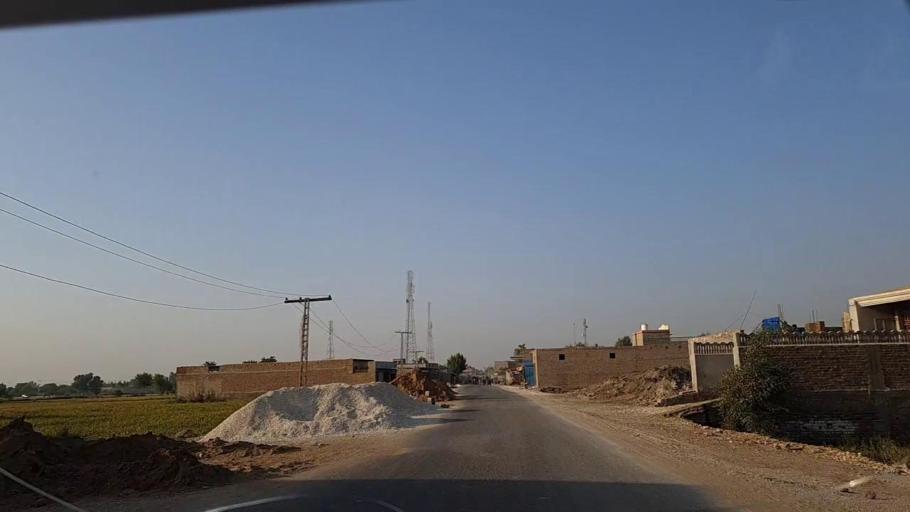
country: PK
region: Sindh
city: Rustam jo Goth
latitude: 27.9610
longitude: 68.8064
